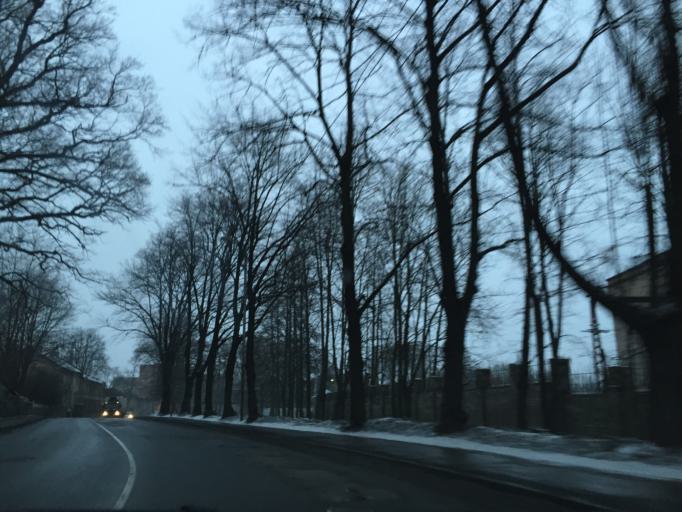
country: LV
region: Riga
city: Riga
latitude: 56.9627
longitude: 24.0712
